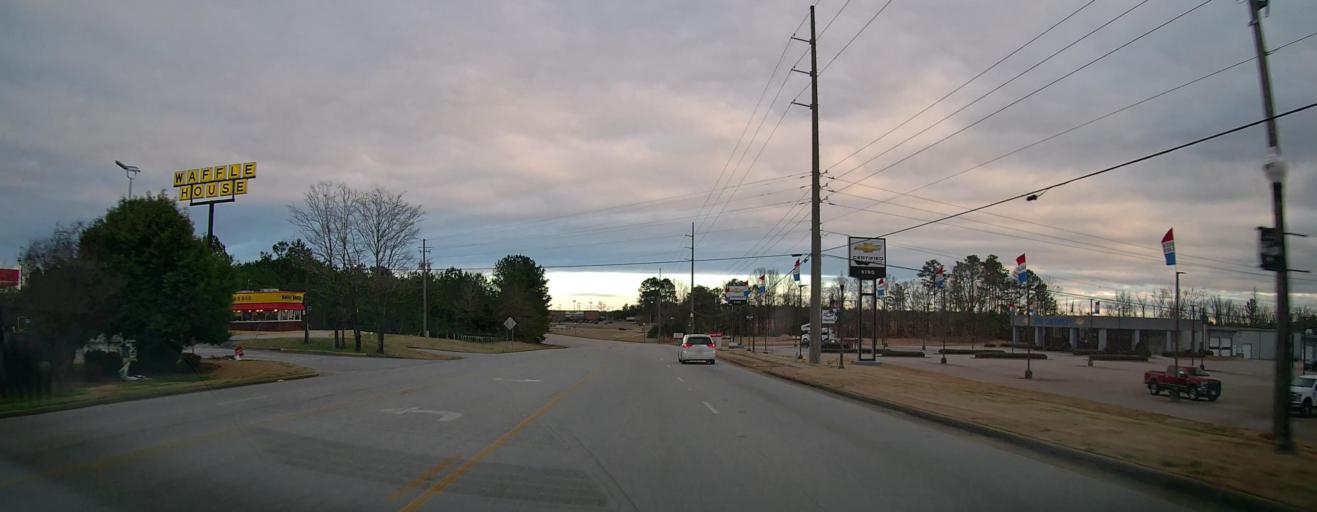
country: US
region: Alabama
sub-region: Chambers County
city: Huguley
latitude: 32.8200
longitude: -85.2116
